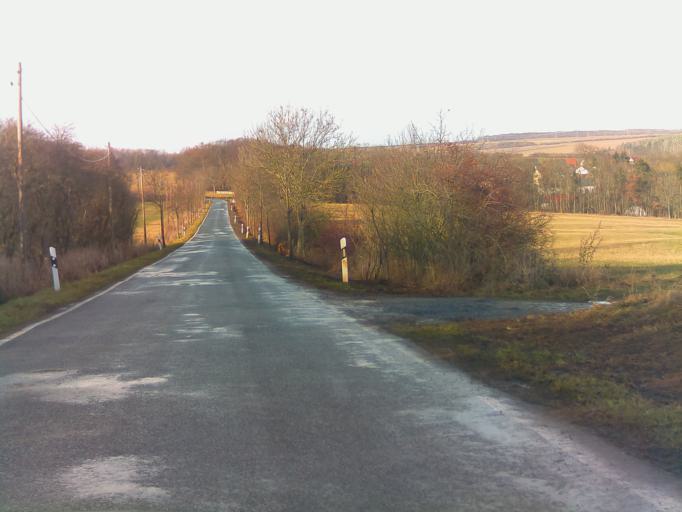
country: DE
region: Thuringia
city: Bad Berka
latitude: 50.9238
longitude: 11.2738
